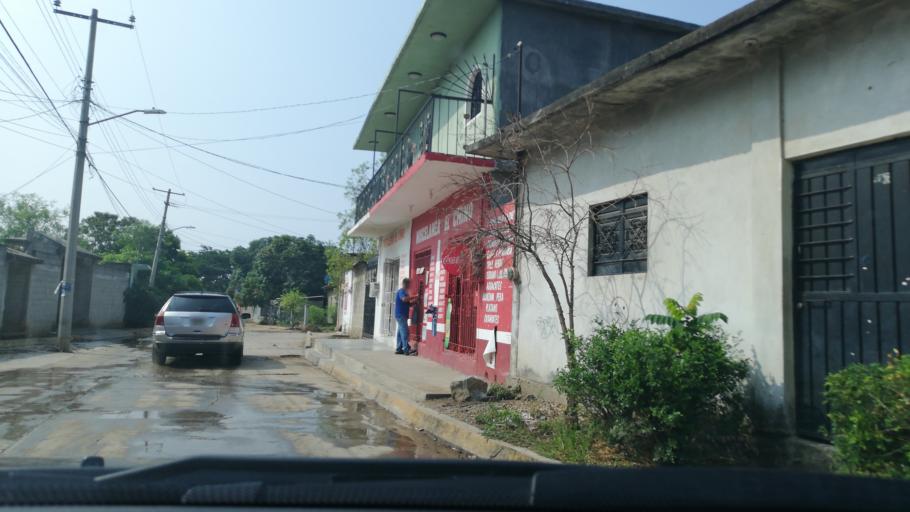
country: MX
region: Oaxaca
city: San Blas Atempa
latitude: 16.3390
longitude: -95.2205
